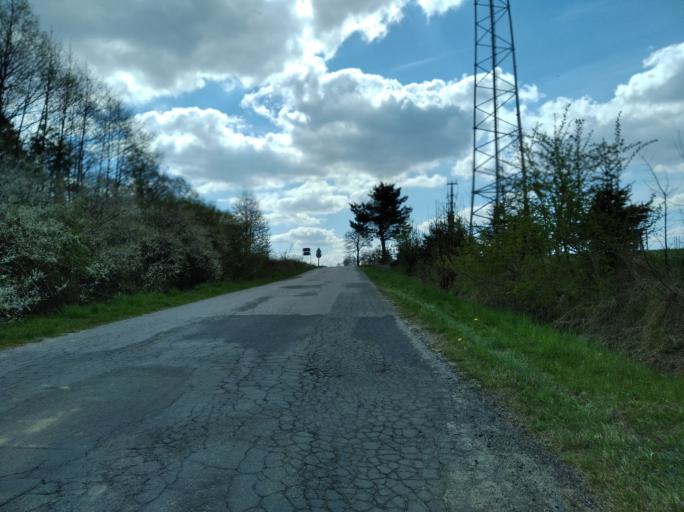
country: PL
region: Subcarpathian Voivodeship
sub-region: Powiat brzozowski
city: Wesola
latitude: 49.7665
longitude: 22.1263
